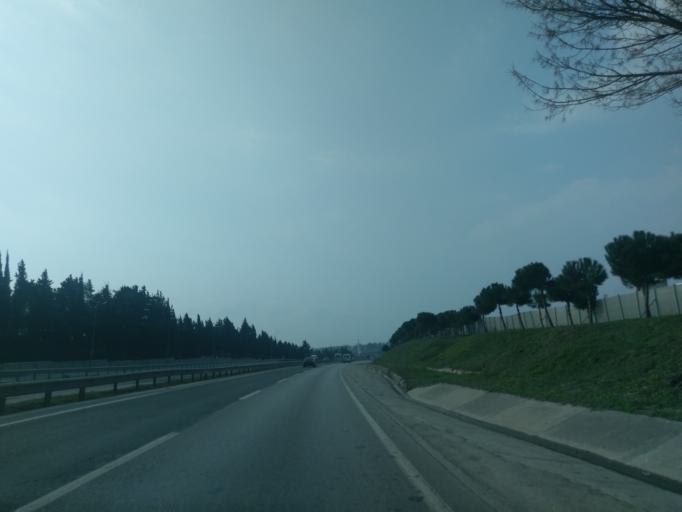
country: TR
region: Istanbul
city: Chekmejeh
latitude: 41.0074
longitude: 28.5086
